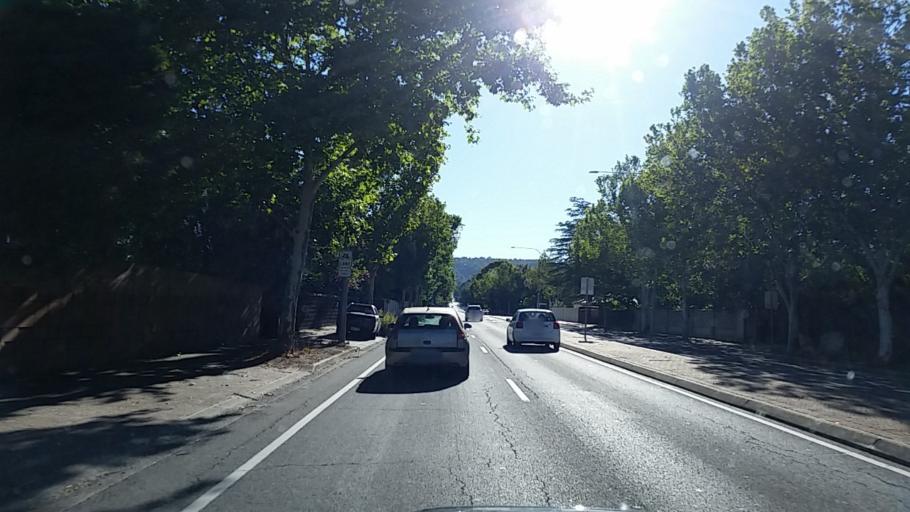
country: AU
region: South Australia
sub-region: Unley
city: Unley Park
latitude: -34.9651
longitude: 138.6138
